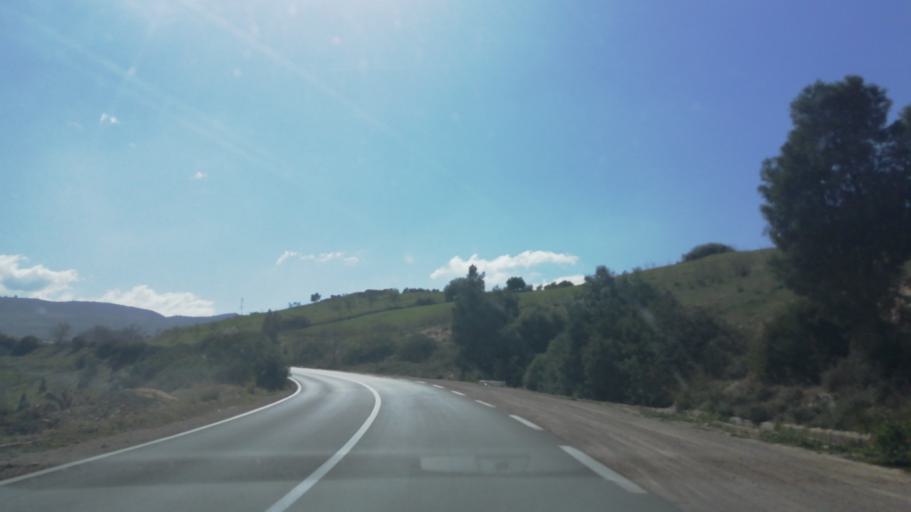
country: DZ
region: Mascara
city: Mascara
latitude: 35.4920
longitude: 0.1371
